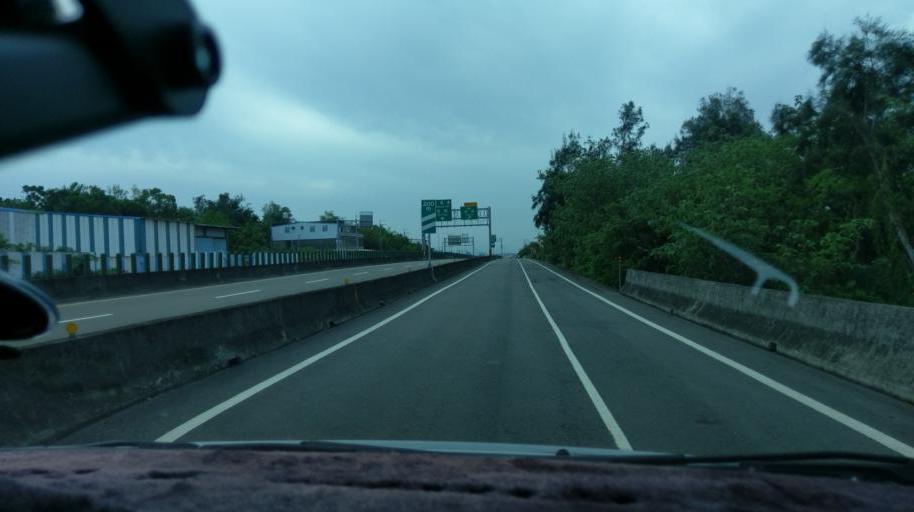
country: TW
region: Taiwan
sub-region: Hsinchu
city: Hsinchu
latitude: 24.7188
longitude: 120.8678
